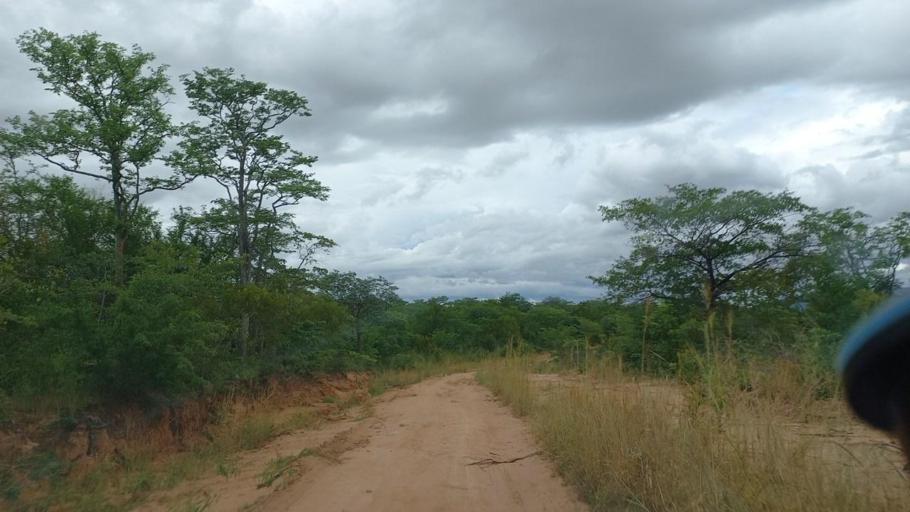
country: ZM
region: Lusaka
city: Luangwa
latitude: -15.5639
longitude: 30.3256
